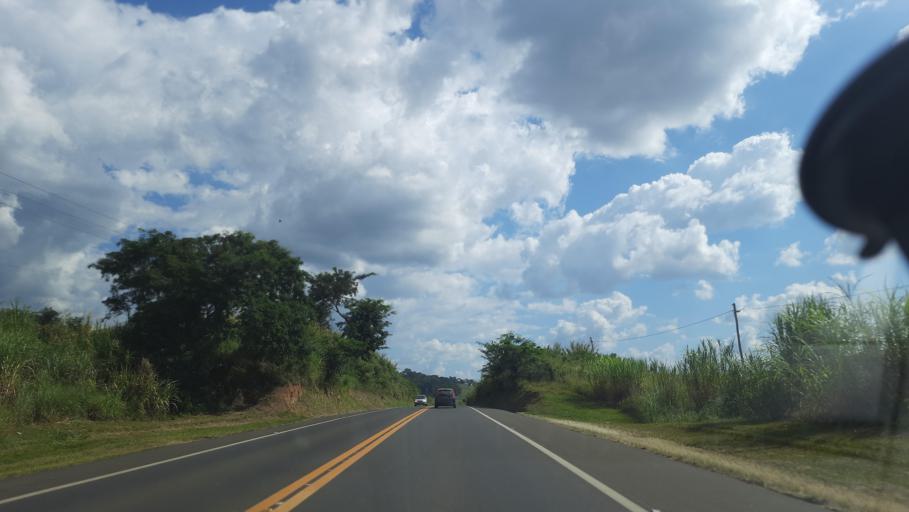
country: BR
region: Sao Paulo
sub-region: Sao Jose Do Rio Pardo
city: Sao Jose do Rio Pardo
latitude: -21.6403
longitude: -46.9059
